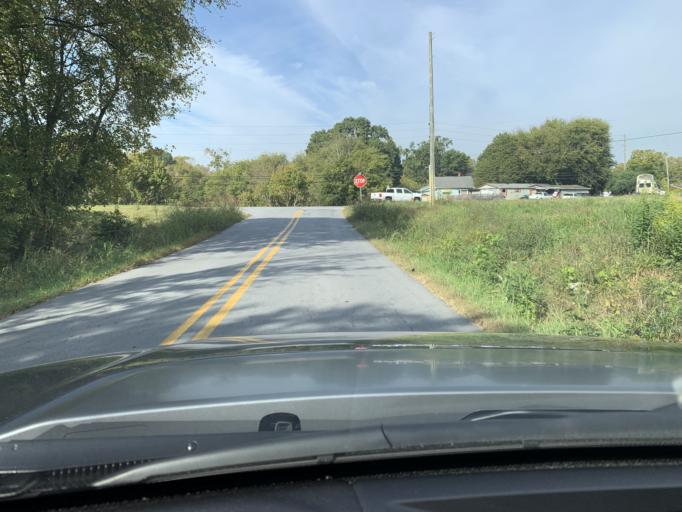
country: US
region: Georgia
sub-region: Polk County
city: Aragon
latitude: 34.0374
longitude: -85.0519
